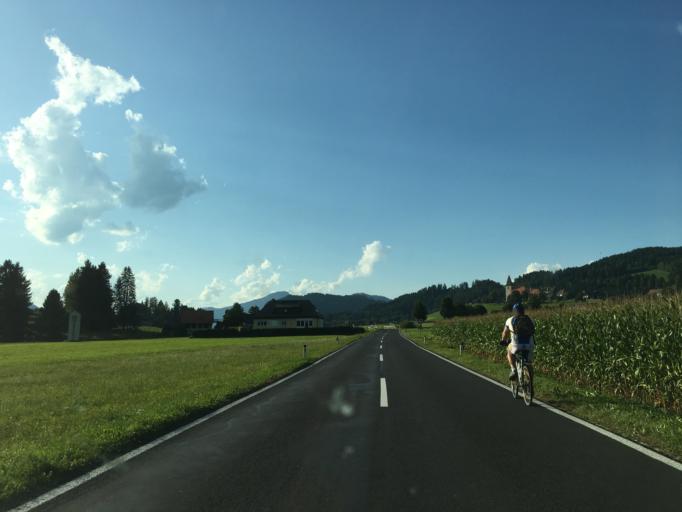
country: AT
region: Styria
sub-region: Politischer Bezirk Murau
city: Mariahof
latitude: 47.0895
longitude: 14.4045
